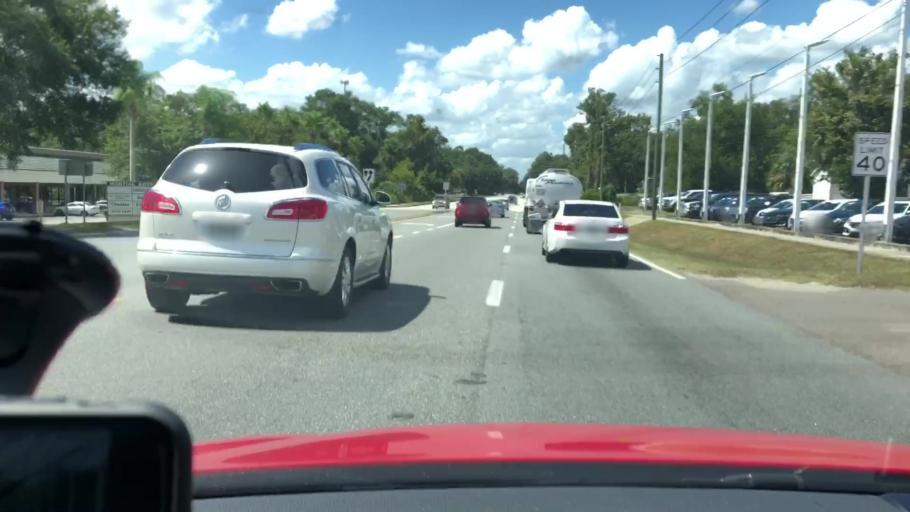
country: US
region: Florida
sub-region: Volusia County
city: De Land Southwest
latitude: 28.9989
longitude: -81.3037
